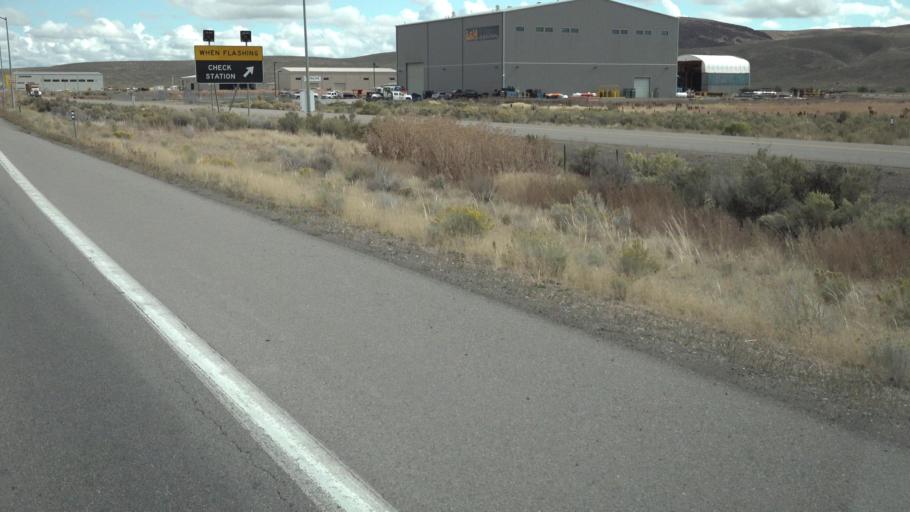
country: US
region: Nevada
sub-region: Elko County
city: Elko
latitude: 40.9401
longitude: -115.6512
